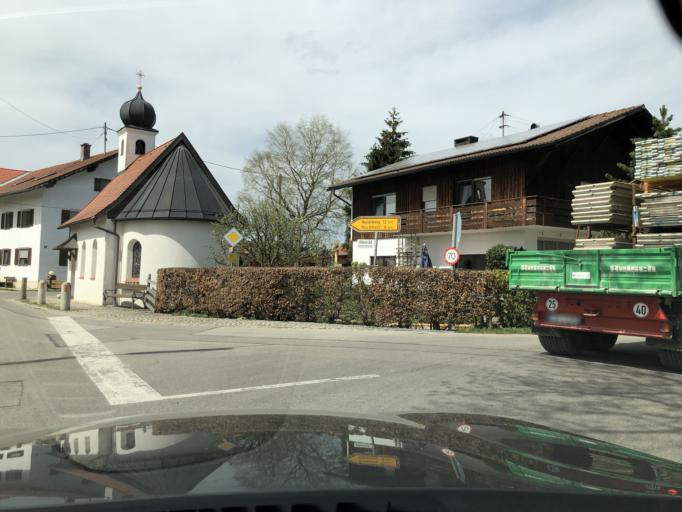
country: DE
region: Bavaria
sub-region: Swabia
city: Lengenwang
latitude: 47.6968
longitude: 10.5884
